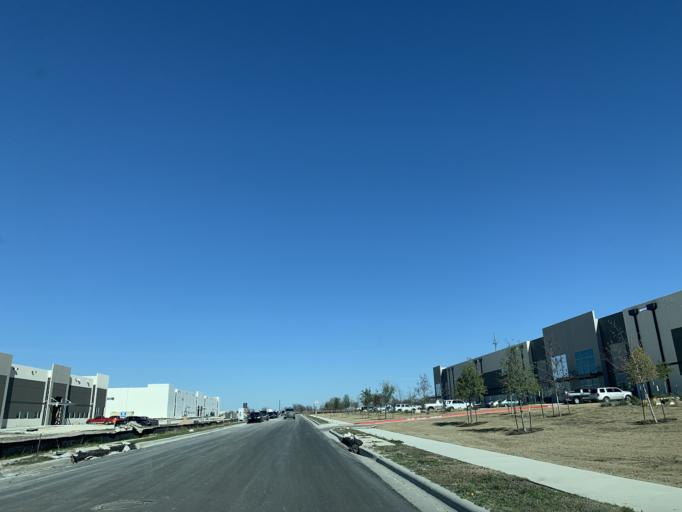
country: US
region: Texas
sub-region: Williamson County
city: Hutto
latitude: 30.5485
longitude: -97.5692
